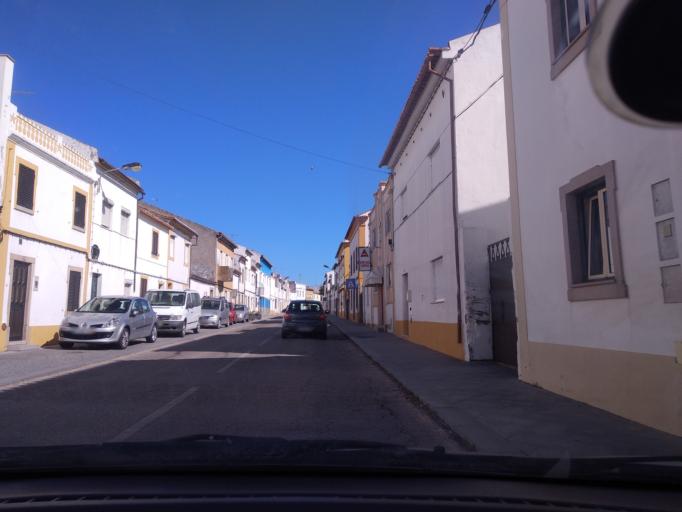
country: PT
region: Portalegre
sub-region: Nisa
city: Nisa
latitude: 39.5123
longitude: -7.6480
